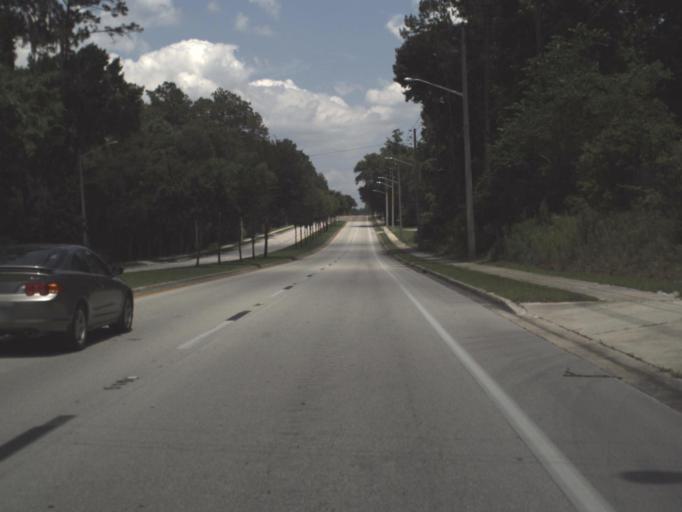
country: US
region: Florida
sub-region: Alachua County
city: Alachua
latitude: 29.6599
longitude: -82.4633
